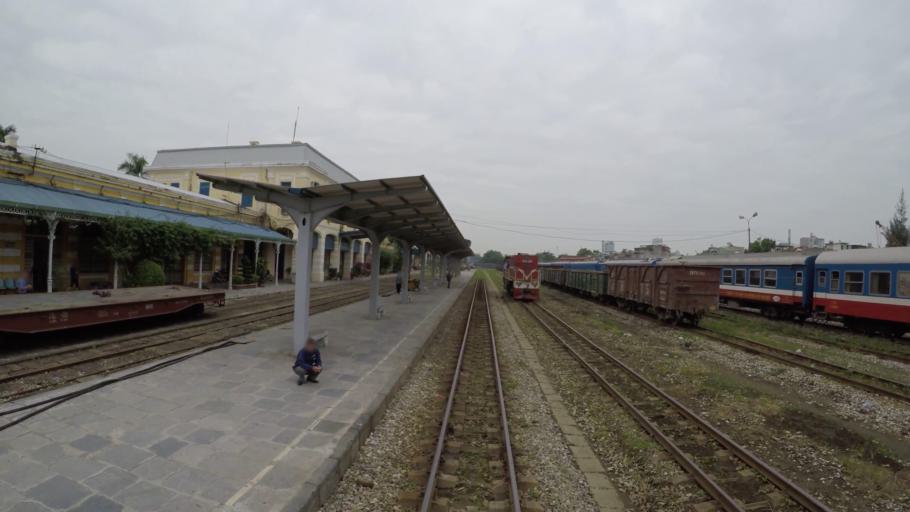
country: VN
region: Hai Phong
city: Haiphong
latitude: 20.8518
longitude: 106.6785
